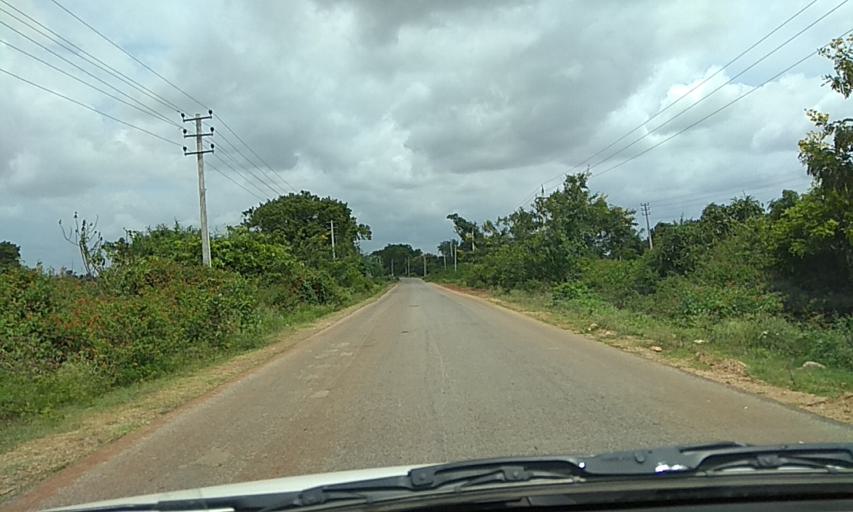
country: IN
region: Karnataka
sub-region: Chamrajnagar
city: Gundlupet
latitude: 11.8026
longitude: 76.7946
